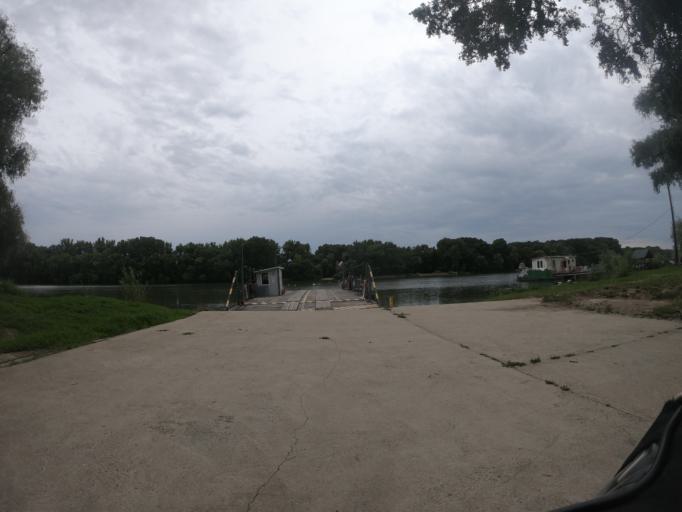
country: HU
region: Hajdu-Bihar
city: Egyek
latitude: 47.6755
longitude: 20.8653
